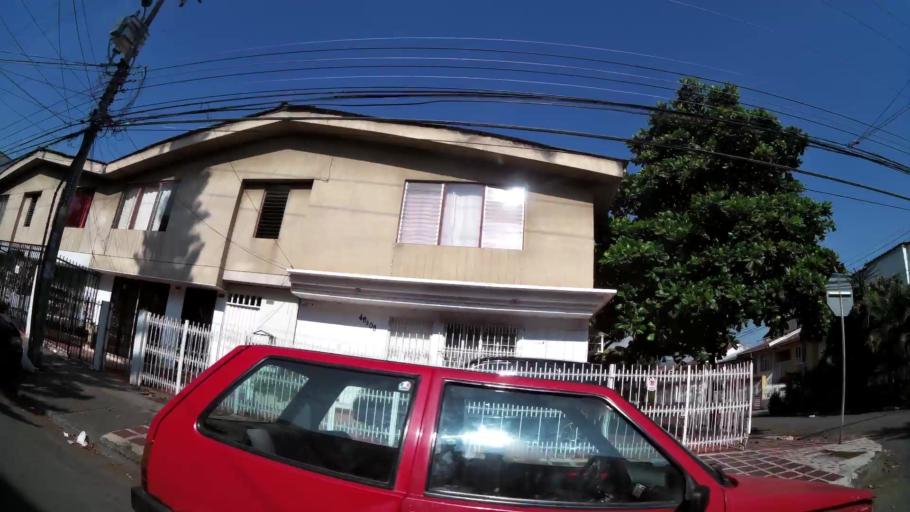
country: CO
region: Valle del Cauca
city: Cali
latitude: 3.4107
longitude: -76.5276
